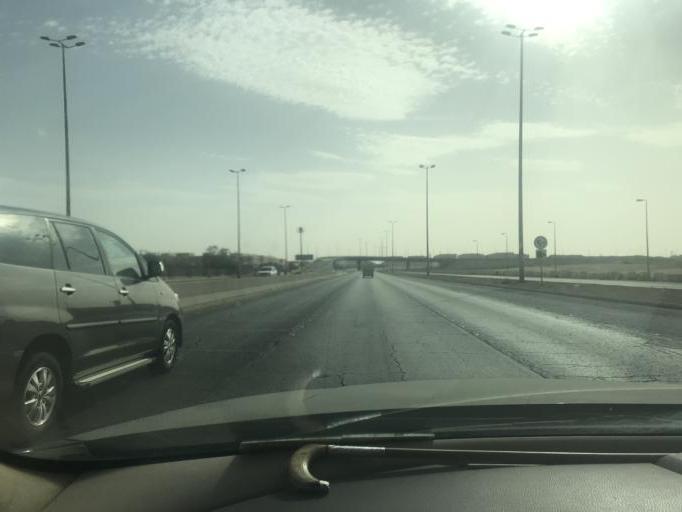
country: SA
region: Ar Riyad
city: Riyadh
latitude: 24.8231
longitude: 46.7132
